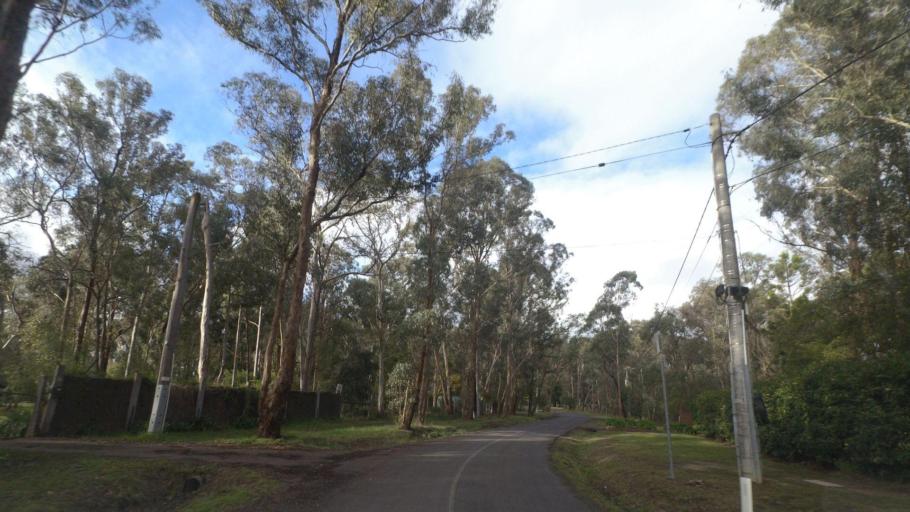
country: AU
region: Victoria
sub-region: Nillumbik
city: North Warrandyte
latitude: -37.7394
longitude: 145.2050
